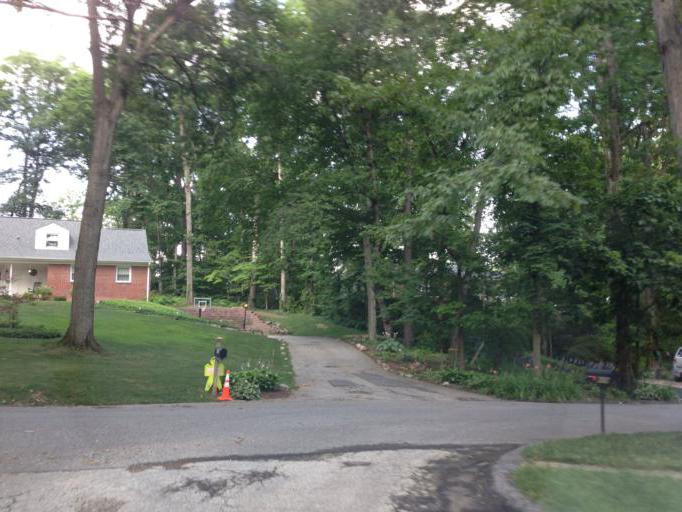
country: US
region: Maryland
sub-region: Baltimore County
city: Towson
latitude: 39.3923
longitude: -76.5881
